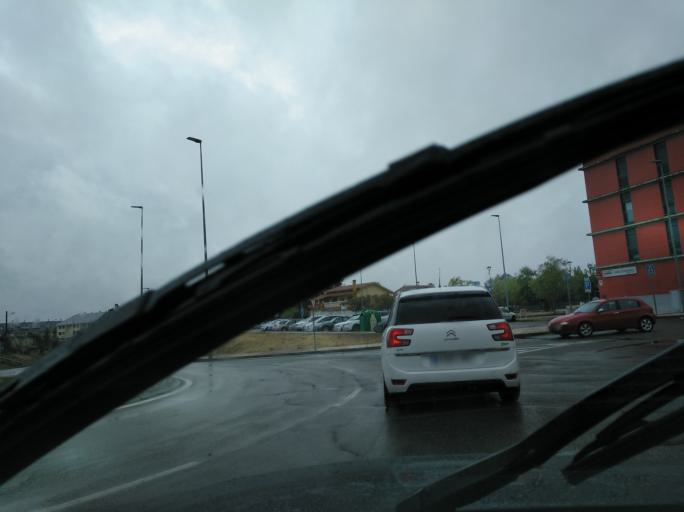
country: ES
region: Extremadura
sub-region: Provincia de Badajoz
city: Badajoz
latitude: 38.8854
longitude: -6.9902
